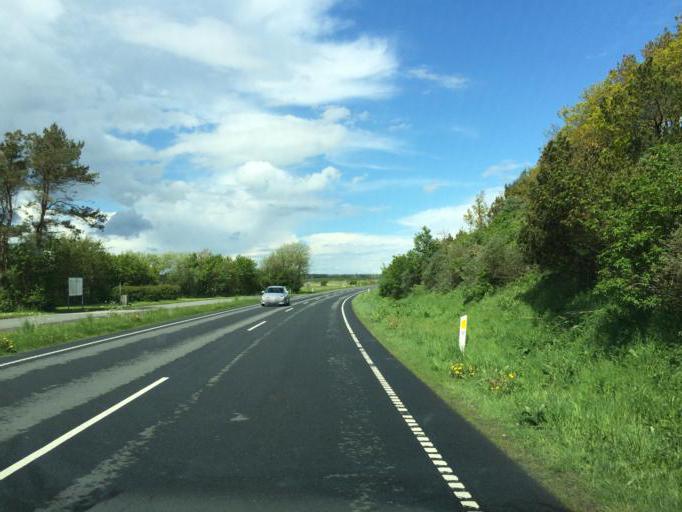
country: DK
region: North Denmark
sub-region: Vesthimmerland Kommune
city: Farso
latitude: 56.6874
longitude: 9.3193
